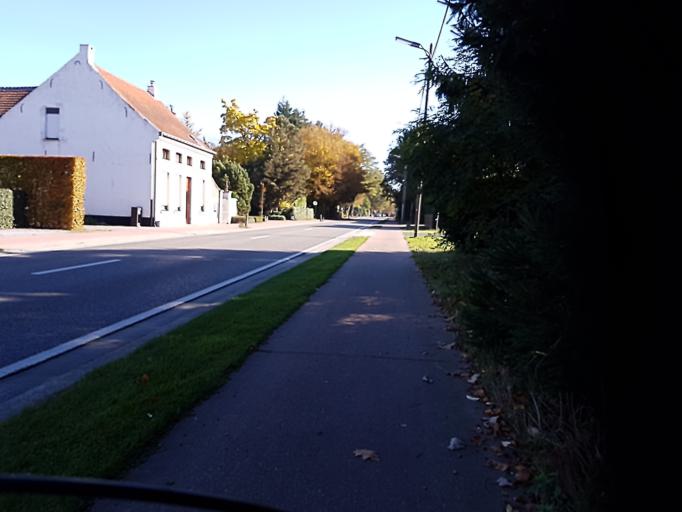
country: BE
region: Flanders
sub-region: Provincie Antwerpen
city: Bonheiden
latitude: 51.0309
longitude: 4.5220
